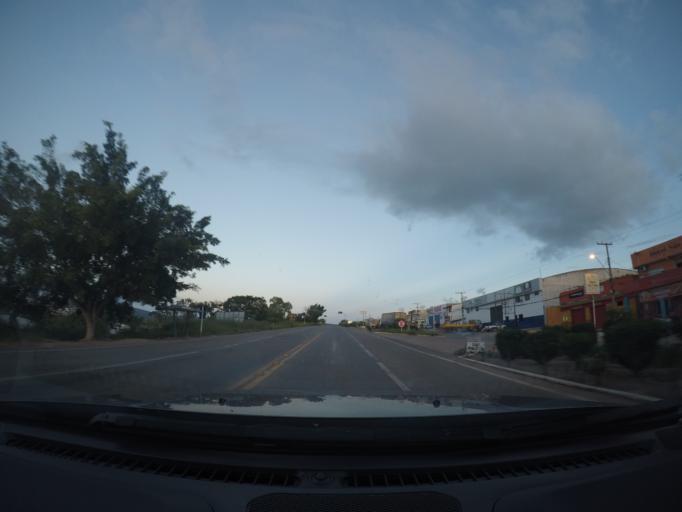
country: BR
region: Bahia
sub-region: Seabra
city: Seabra
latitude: -12.4273
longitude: -41.7688
